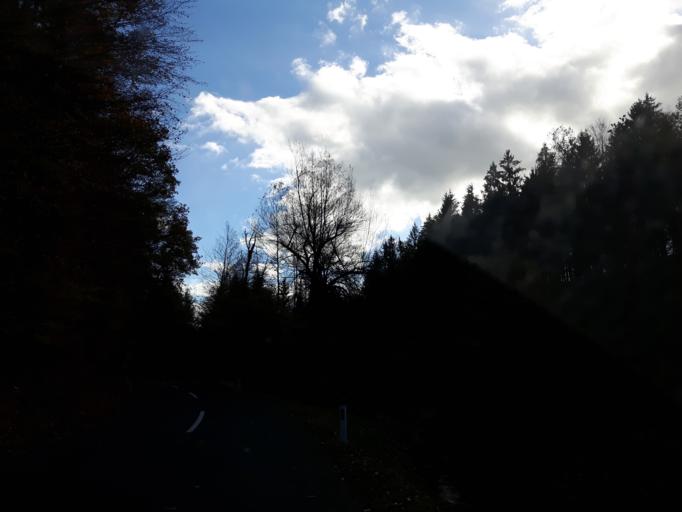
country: AT
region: Styria
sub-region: Politischer Bezirk Leibnitz
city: Oberhaag
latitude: 46.6977
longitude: 15.3062
